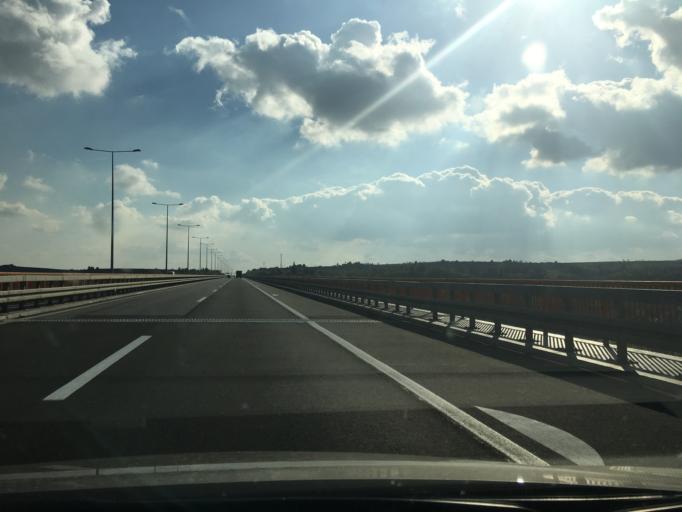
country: RS
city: Beska
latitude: 45.1735
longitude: 20.0790
